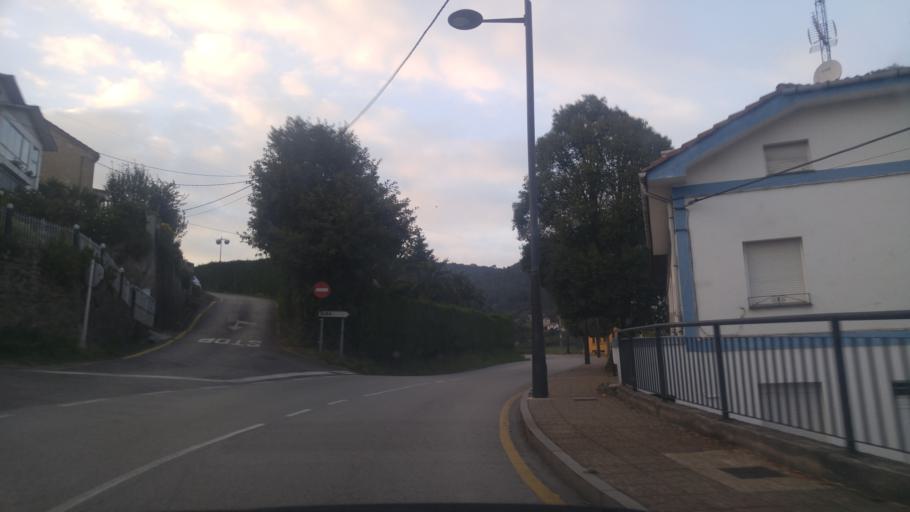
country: ES
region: Asturias
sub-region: Province of Asturias
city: Oviedo
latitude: 43.3733
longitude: -5.8622
